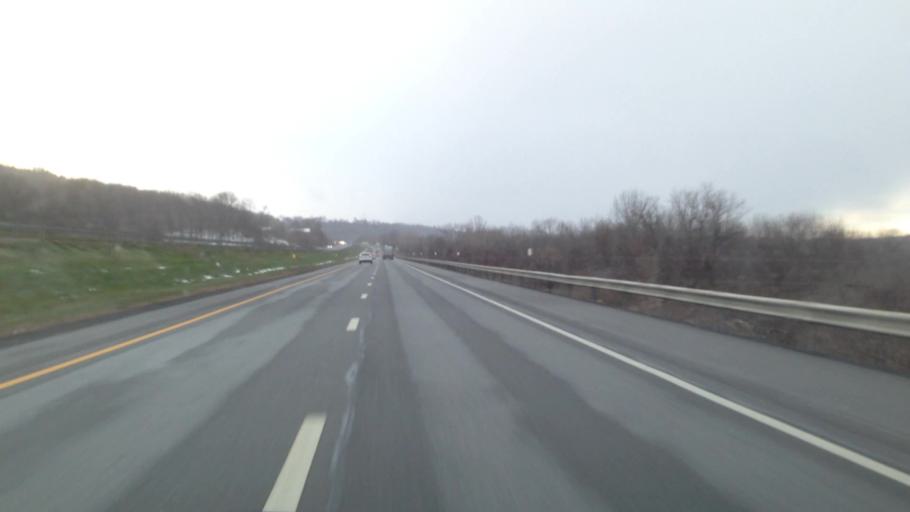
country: US
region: New York
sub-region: Montgomery County
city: Saint Johnsville
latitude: 42.9908
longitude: -74.6889
